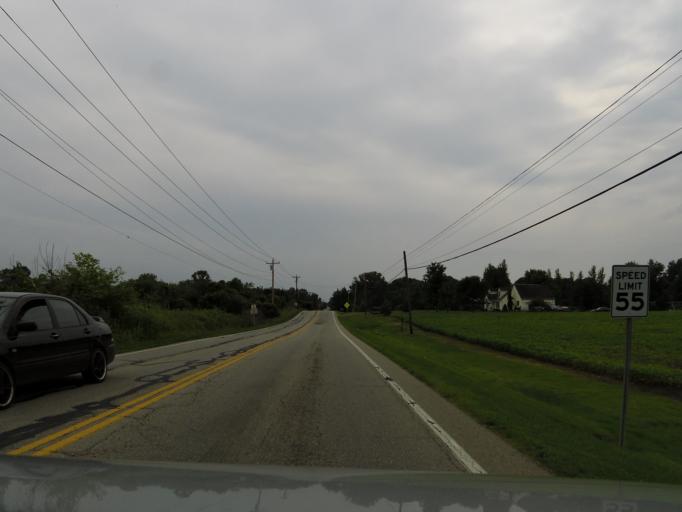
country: US
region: Ohio
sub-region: Brown County
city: Mount Orab
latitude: 38.9976
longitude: -83.9214
